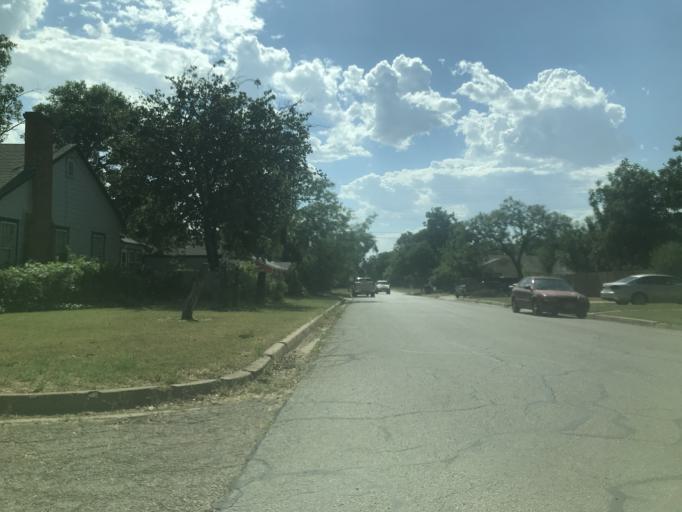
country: US
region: Texas
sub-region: Taylor County
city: Abilene
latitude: 32.4357
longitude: -99.7492
